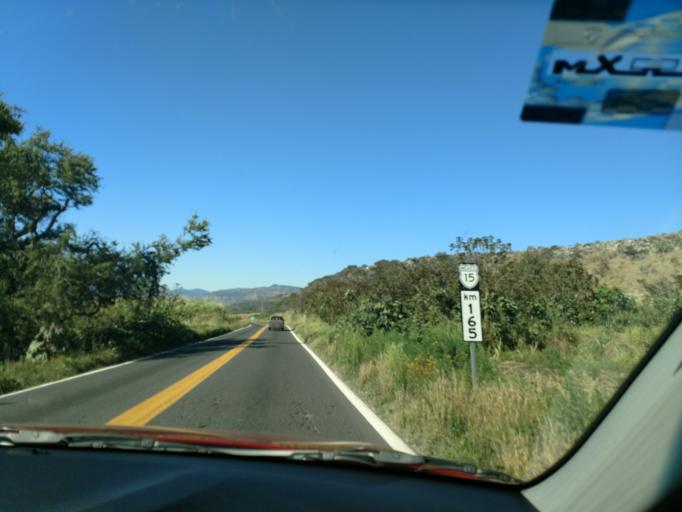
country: MX
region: Nayarit
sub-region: Ahuacatlan
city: Ahuacatlan
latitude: 21.1089
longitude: -104.5874
